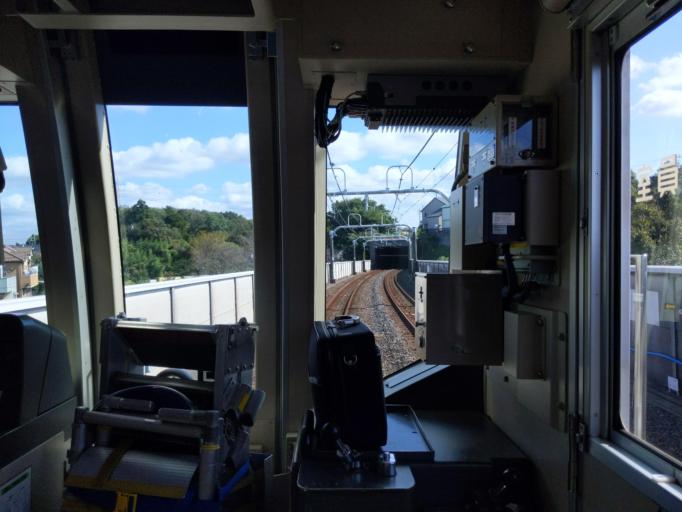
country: JP
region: Chiba
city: Yotsukaido
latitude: 35.7216
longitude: 140.1228
